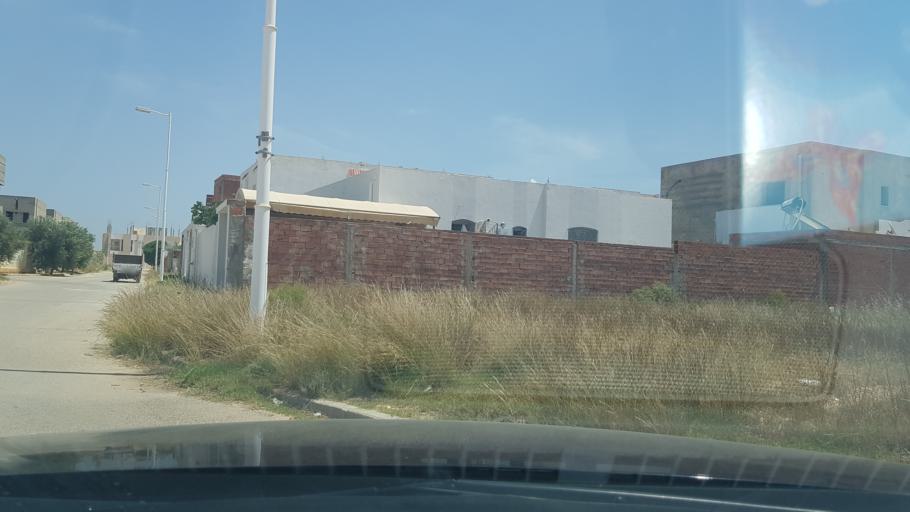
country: TN
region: Safaqis
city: Al Qarmadah
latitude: 34.8390
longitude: 10.7586
